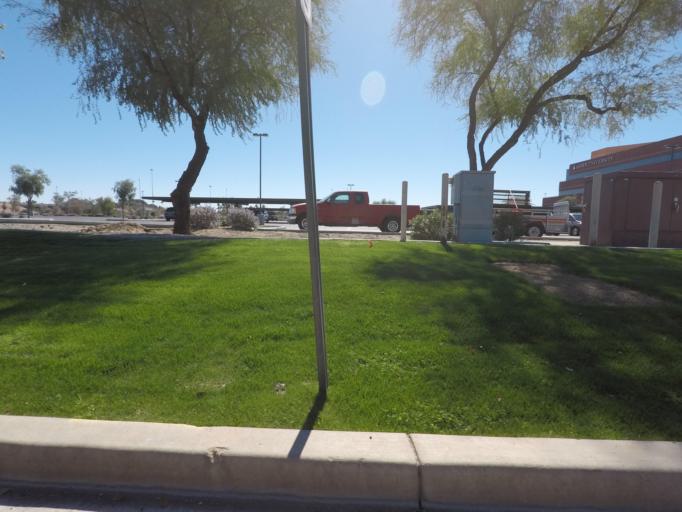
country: US
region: Arizona
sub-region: Maricopa County
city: Tempe Junction
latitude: 33.4129
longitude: -111.9805
